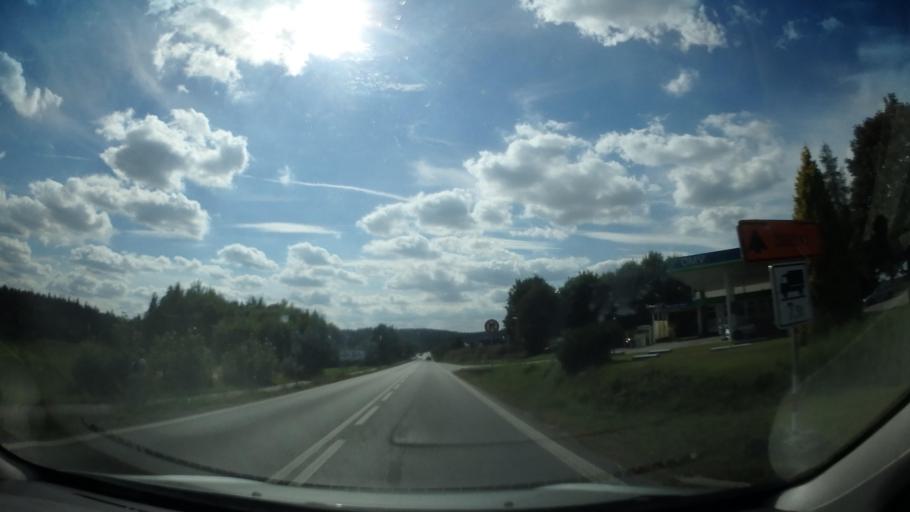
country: CZ
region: Vysocina
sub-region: Okres Zd'ar nad Sazavou
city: Zd'ar nad Sazavou
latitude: 49.5655
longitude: 15.9202
